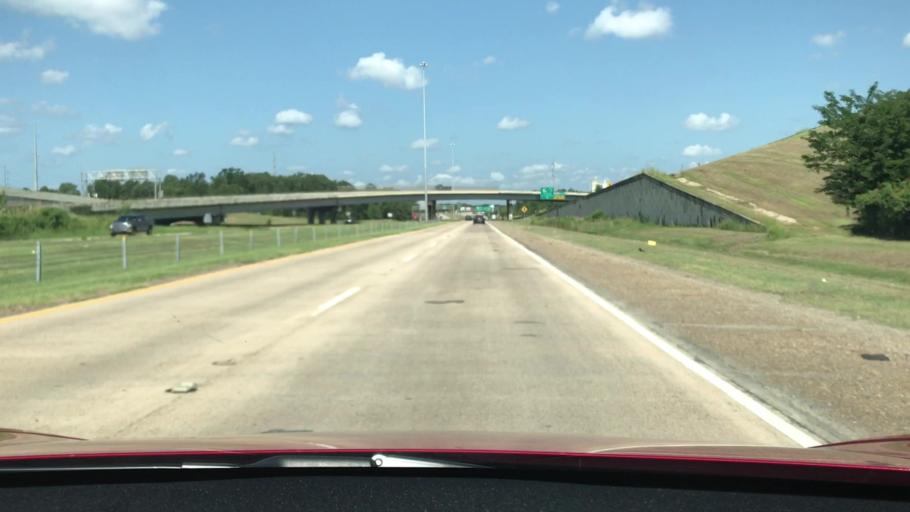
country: US
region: Louisiana
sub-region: Bossier Parish
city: Bossier City
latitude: 32.4194
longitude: -93.7511
